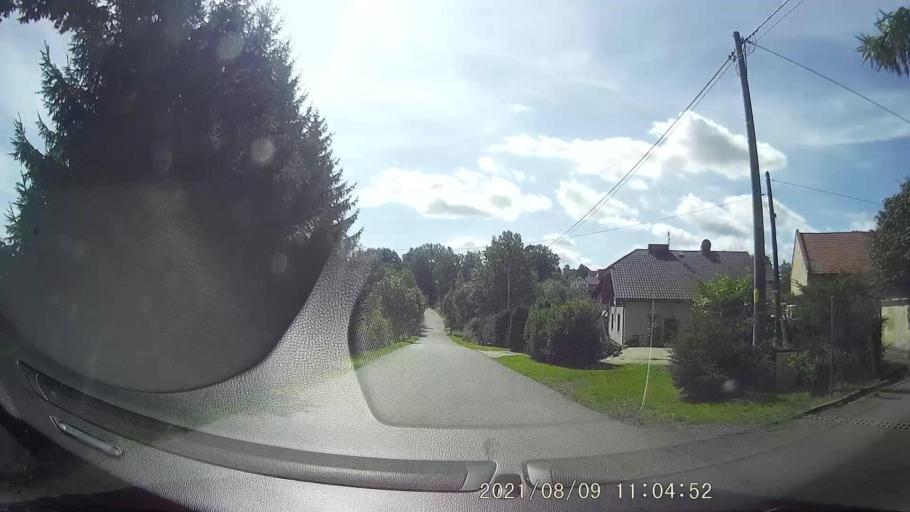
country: PL
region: Lower Silesian Voivodeship
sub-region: Powiat klodzki
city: Bozkow
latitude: 50.4621
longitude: 16.5748
